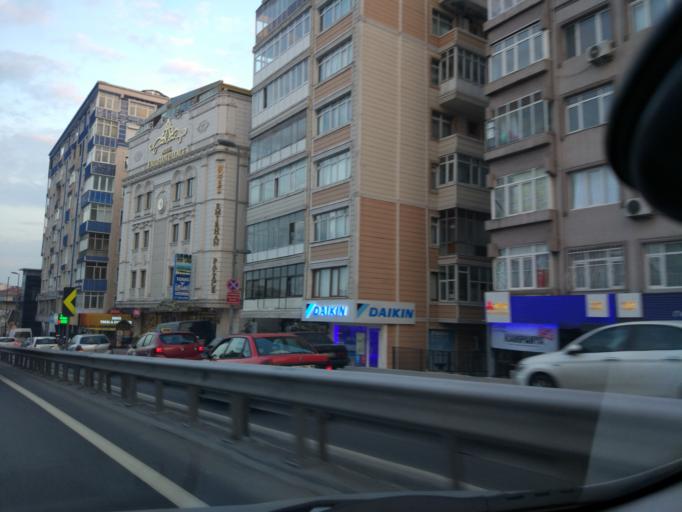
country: TR
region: Istanbul
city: Yakuplu
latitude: 40.9777
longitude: 28.7443
